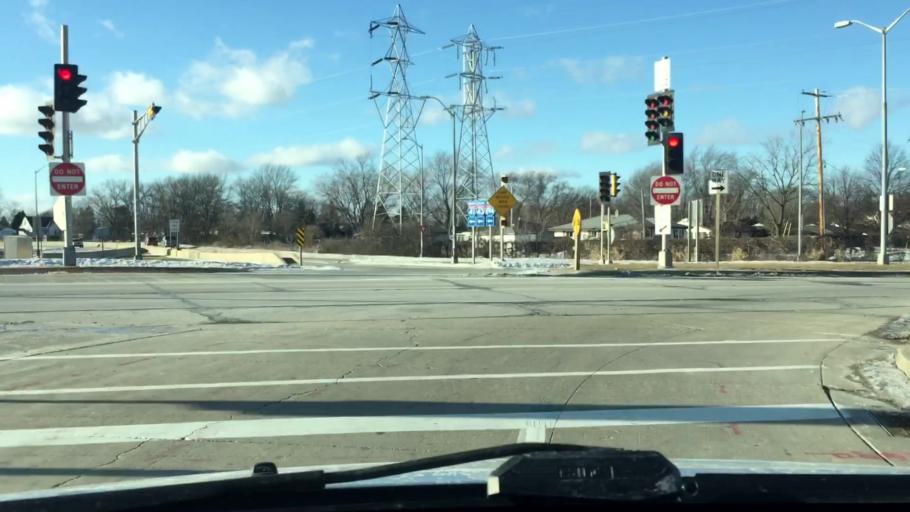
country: US
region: Wisconsin
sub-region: Milwaukee County
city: Greendale
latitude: 42.9625
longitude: -87.9682
